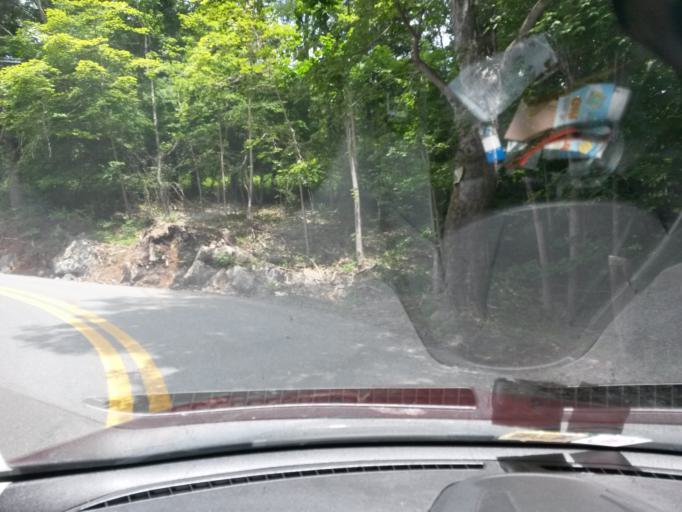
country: US
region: West Virginia
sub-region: Monroe County
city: Union
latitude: 37.5351
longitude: -80.5382
